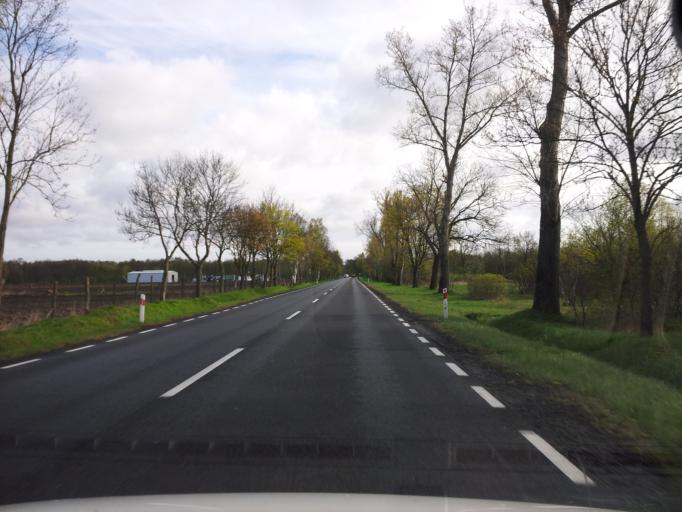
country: PL
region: Lubusz
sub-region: Powiat zielonogorski
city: Swidnica
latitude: 51.8595
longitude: 15.3577
